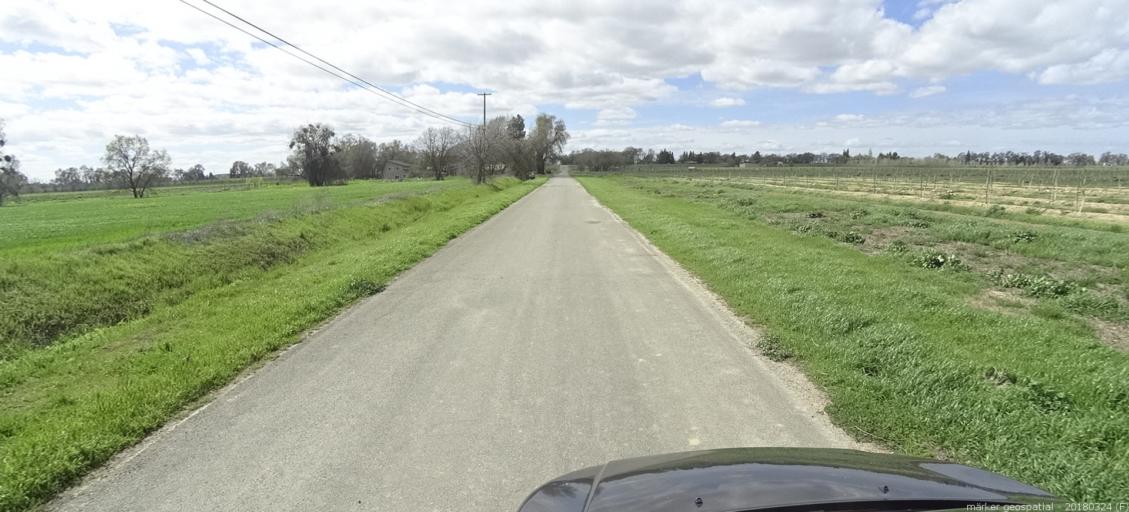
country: US
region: California
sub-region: Yolo County
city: West Sacramento
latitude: 38.6854
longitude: -121.6224
